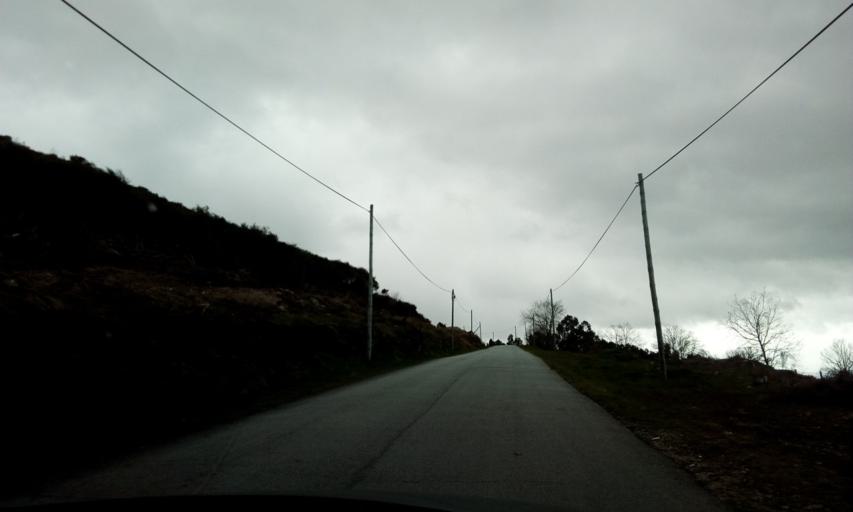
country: PT
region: Guarda
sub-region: Fornos de Algodres
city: Fornos de Algodres
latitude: 40.6368
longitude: -7.6018
